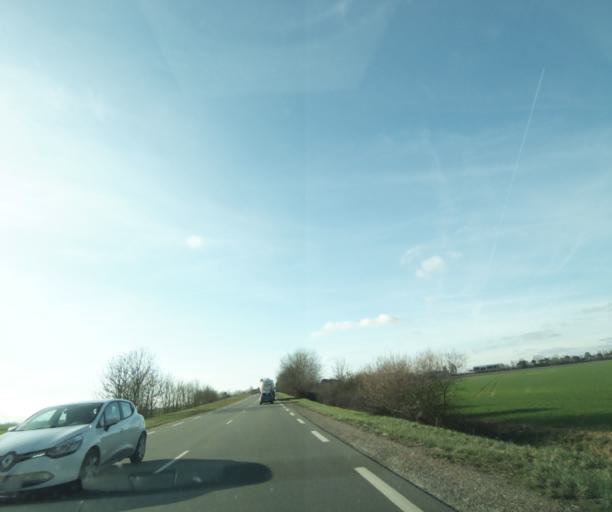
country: FR
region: Ile-de-France
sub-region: Departement des Yvelines
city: Ablis
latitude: 48.4732
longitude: 1.8597
